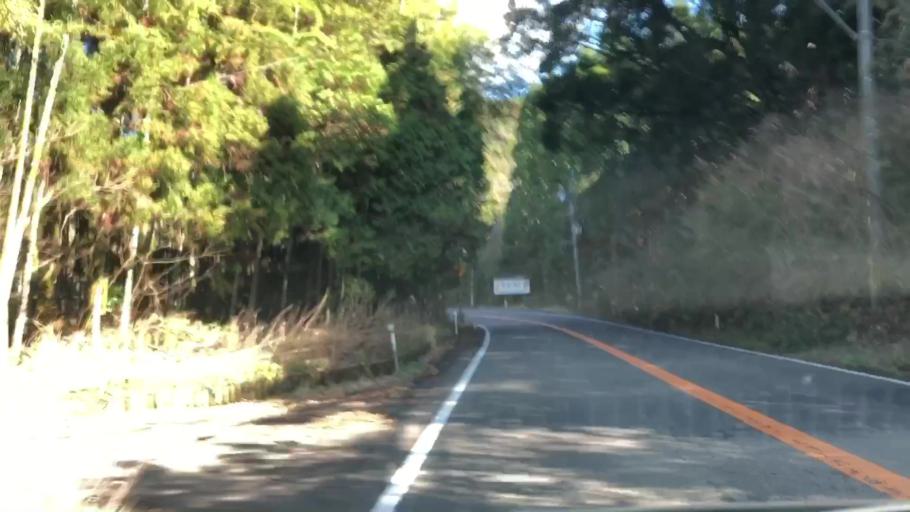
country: JP
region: Kagoshima
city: Satsumasendai
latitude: 31.8531
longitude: 130.4283
